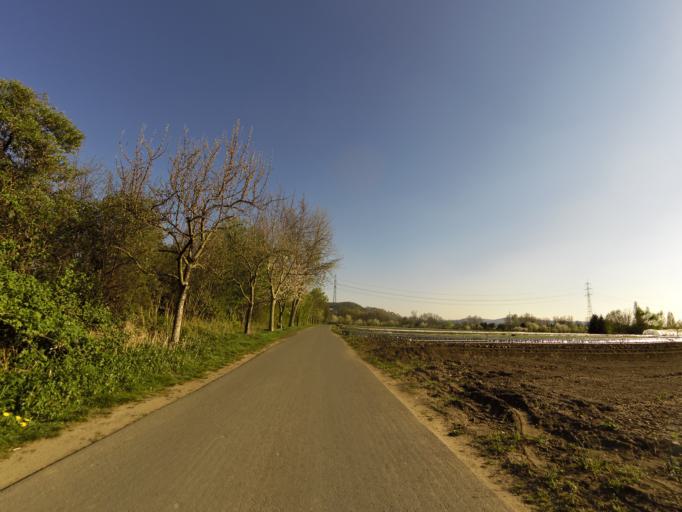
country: DE
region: Rheinland-Pfalz
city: Niederwerth
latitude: 50.3916
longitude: 7.6140
